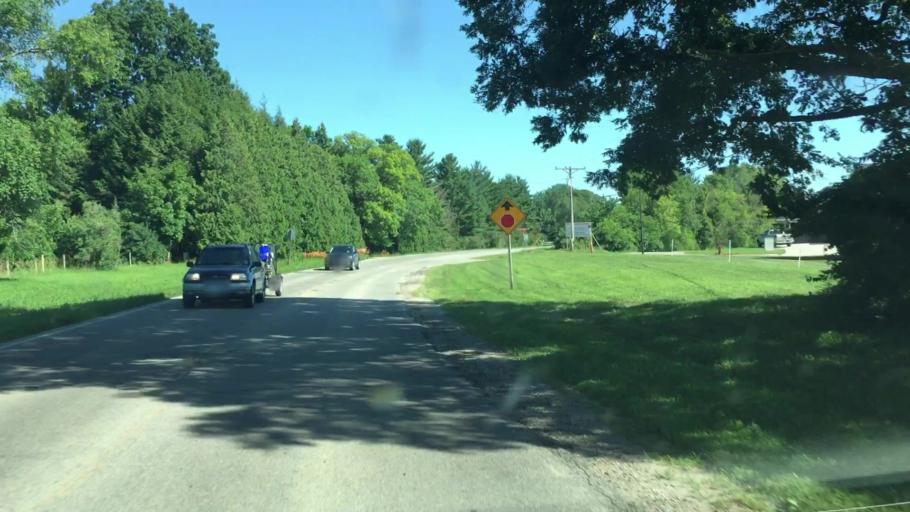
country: US
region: Iowa
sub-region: Linn County
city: Ely
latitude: 41.8368
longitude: -91.6372
